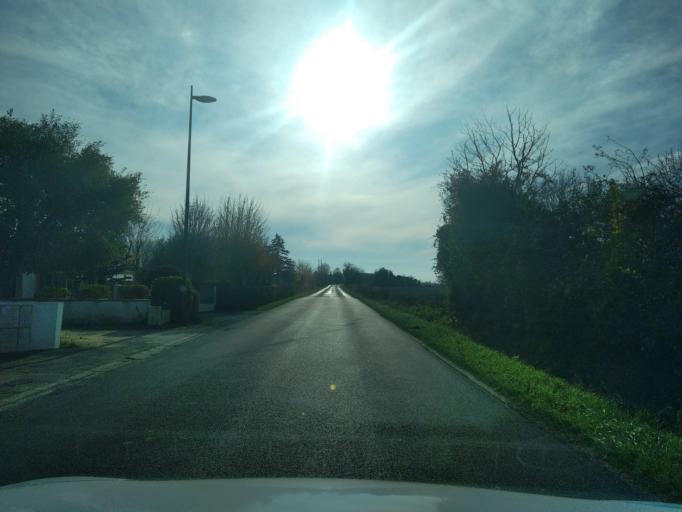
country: FR
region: Pays de la Loire
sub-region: Departement de la Vendee
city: Maillezais
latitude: 46.3661
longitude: -0.7420
